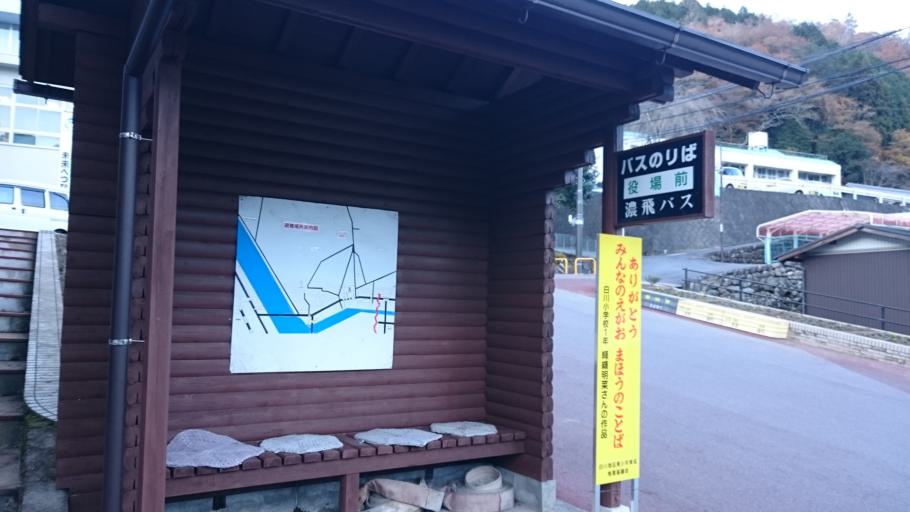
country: JP
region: Gifu
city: Mitake
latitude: 35.5815
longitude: 137.1880
